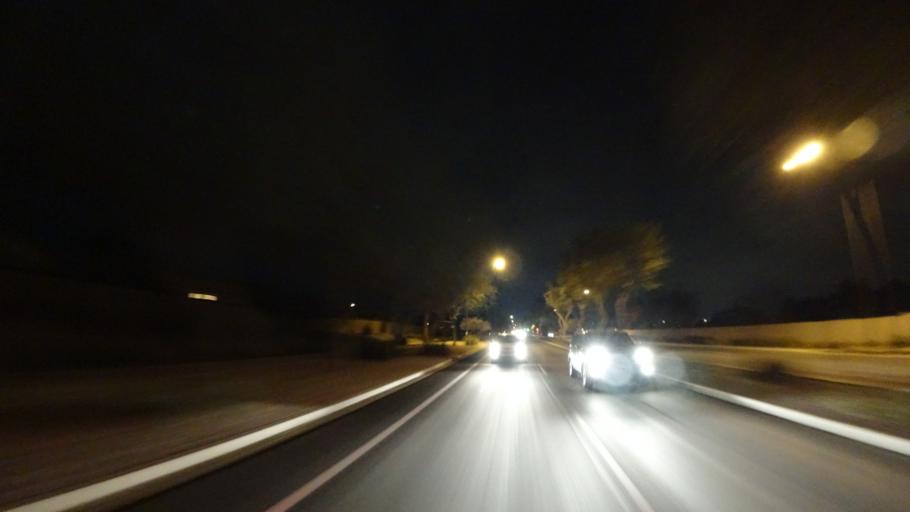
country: US
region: Arizona
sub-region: Maricopa County
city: Queen Creek
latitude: 33.2925
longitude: -111.7097
